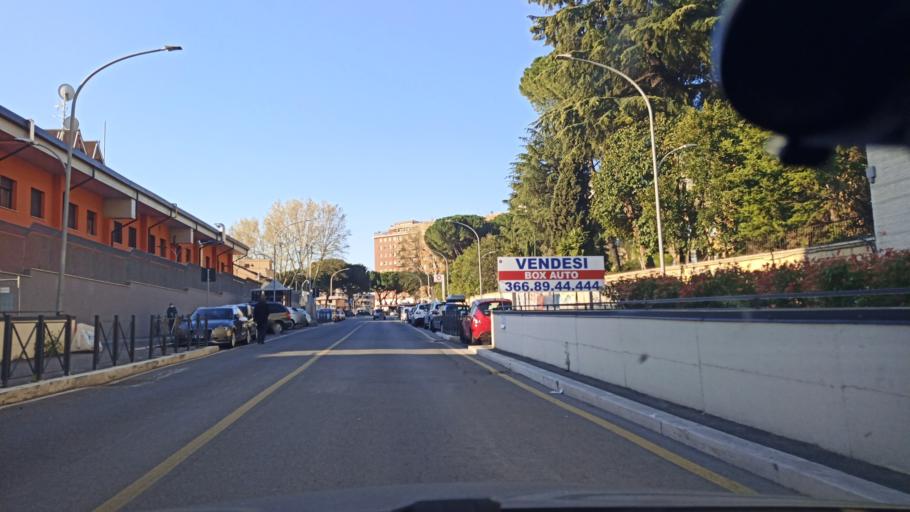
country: IT
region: Latium
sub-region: Citta metropolitana di Roma Capitale
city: Rome
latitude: 41.8780
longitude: 12.5107
